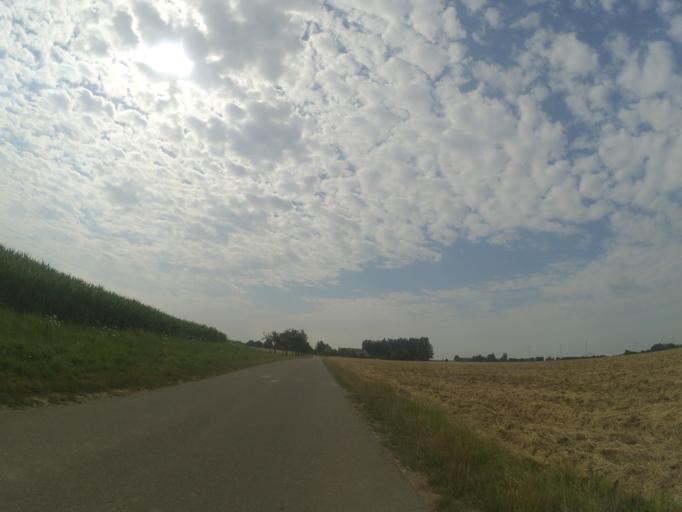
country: DE
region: Baden-Wuerttemberg
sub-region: Tuebingen Region
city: Dornstadt
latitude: 48.4907
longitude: 9.9012
